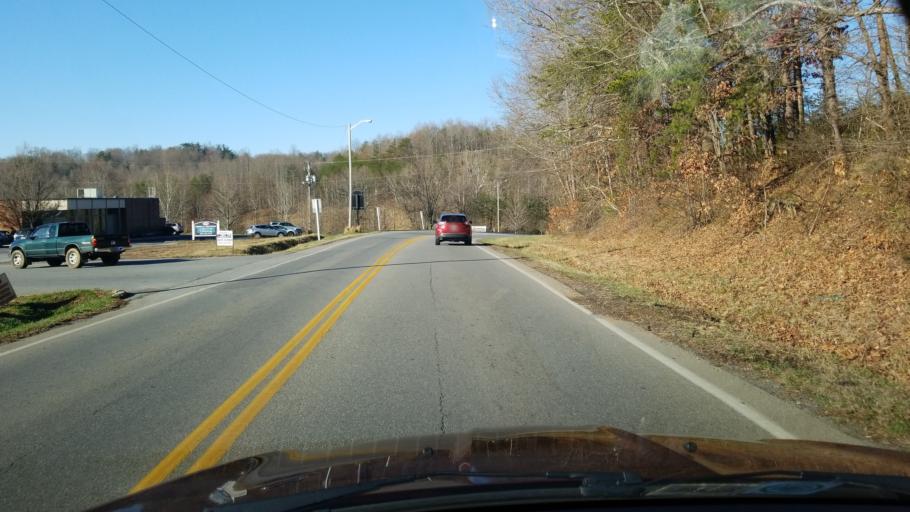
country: US
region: Virginia
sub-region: Franklin County
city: Rocky Mount
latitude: 36.9909
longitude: -79.9010
